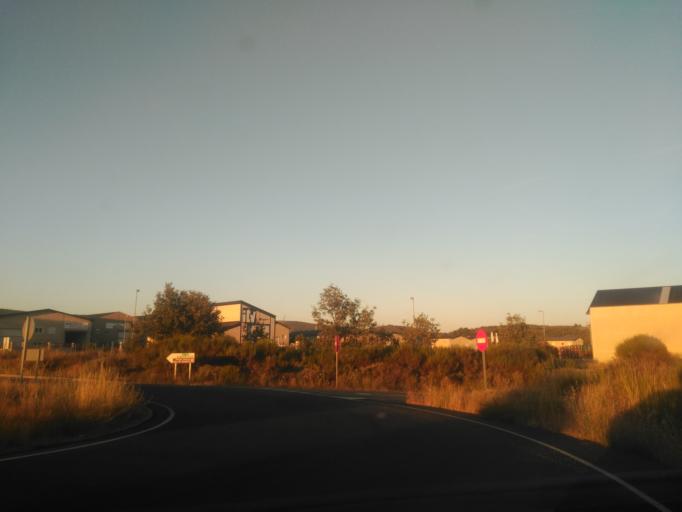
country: ES
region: Castille and Leon
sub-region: Provincia de Zamora
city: Puebla de Sanabria
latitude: 42.0600
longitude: -6.6241
